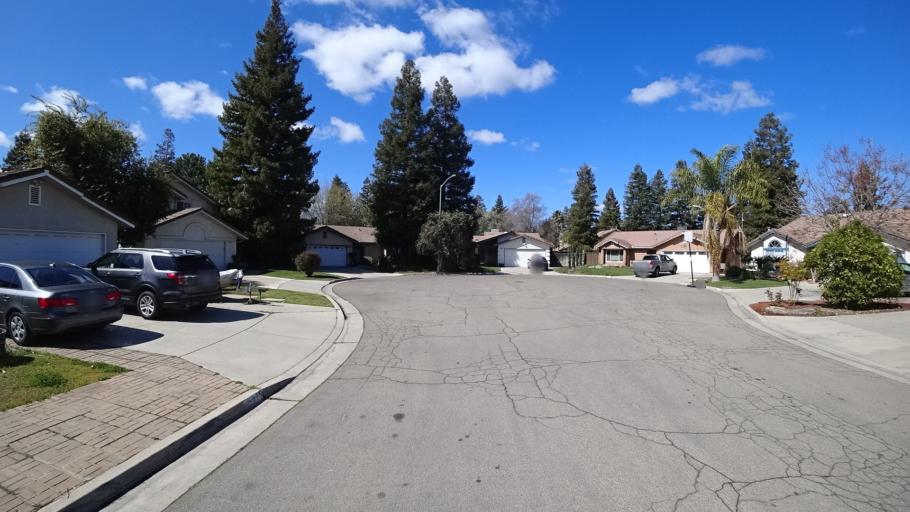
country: US
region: California
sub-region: Fresno County
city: West Park
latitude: 36.8228
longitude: -119.8903
